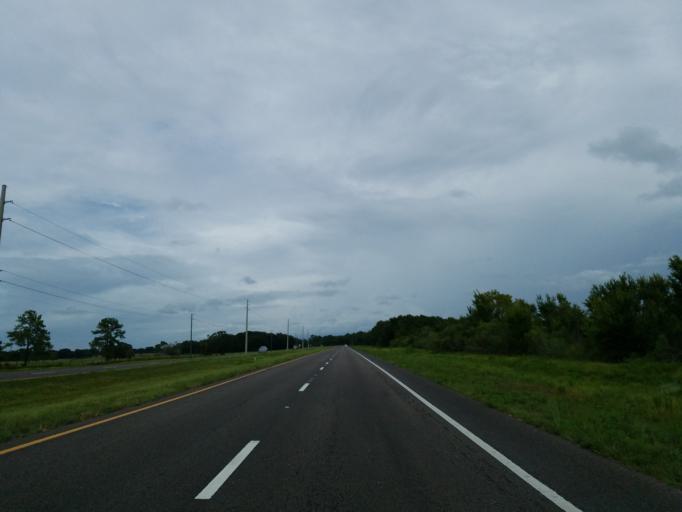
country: US
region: Florida
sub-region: Sumter County
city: Wildwood
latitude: 28.8614
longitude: -82.1618
